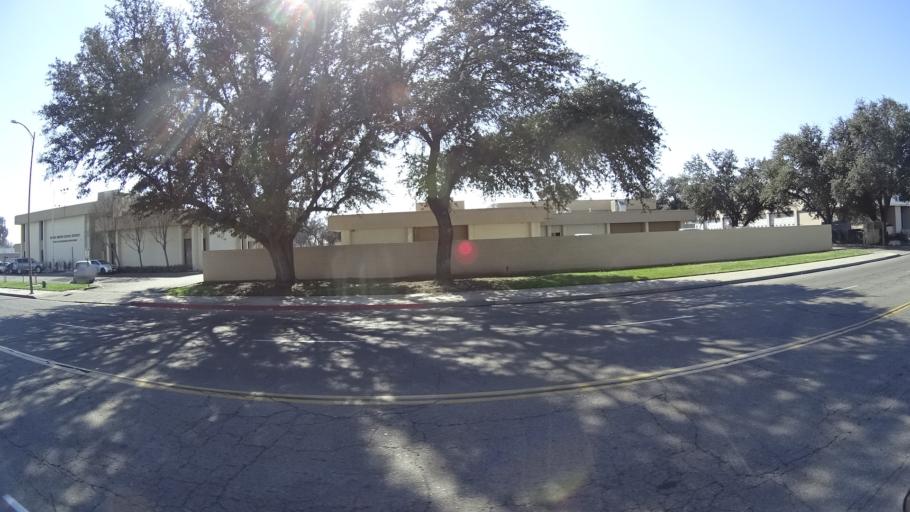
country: US
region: California
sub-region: Fresno County
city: Fresno
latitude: 36.7381
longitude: -119.8052
